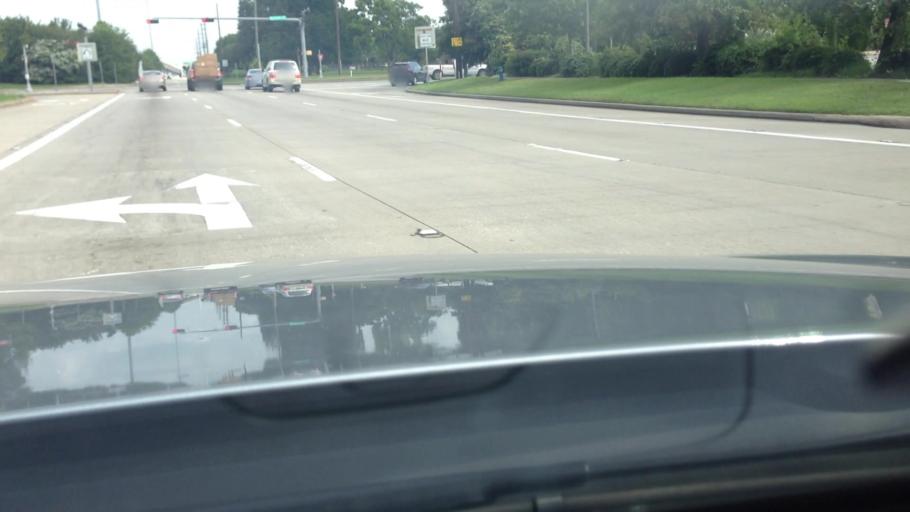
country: US
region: Texas
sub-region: Harris County
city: Hudson
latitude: 29.9530
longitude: -95.5366
